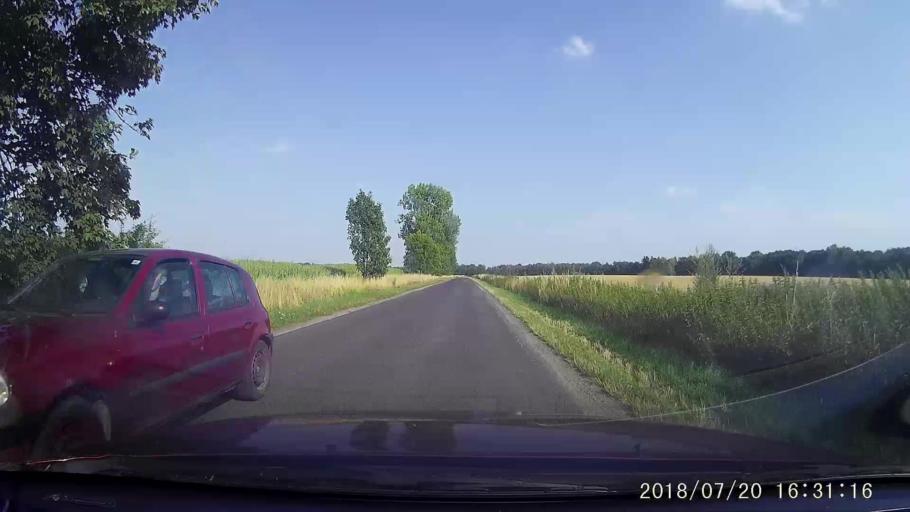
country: PL
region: Lower Silesian Voivodeship
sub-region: Powiat zgorzelecki
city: Sulikow
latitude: 51.1002
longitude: 15.0724
